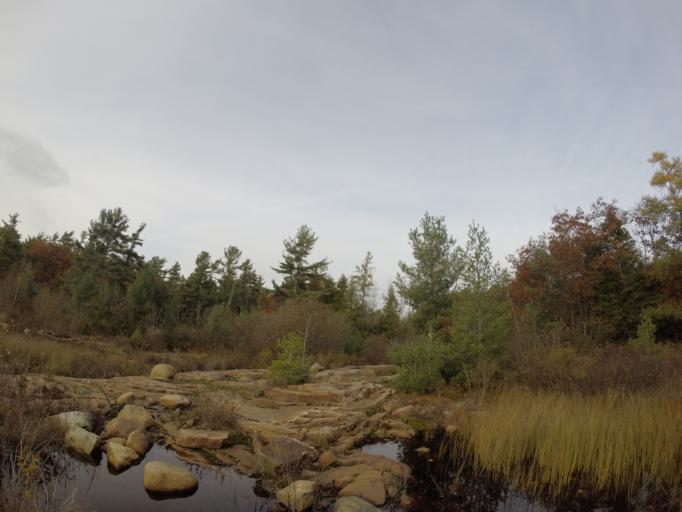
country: CA
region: Ontario
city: Espanola
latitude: 45.9704
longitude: -81.4945
